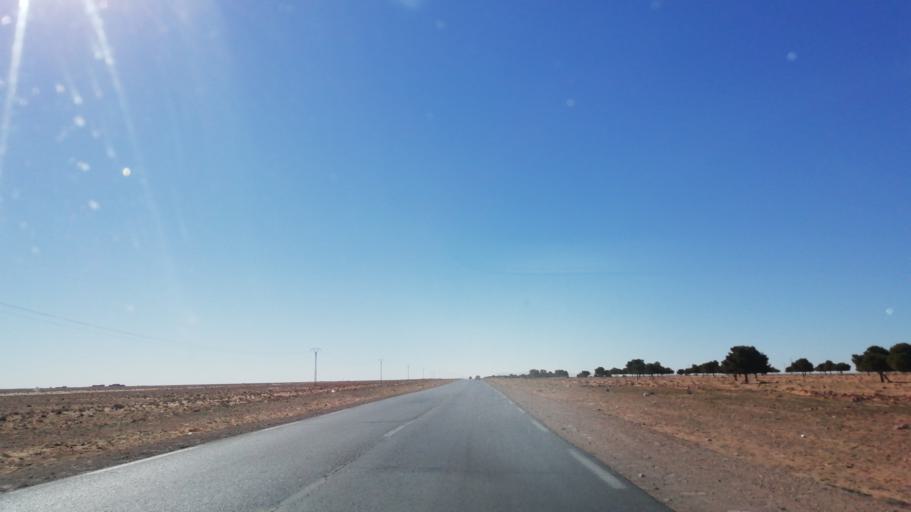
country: DZ
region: Saida
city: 'Ain el Hadjar
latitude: 33.9939
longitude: 0.0382
